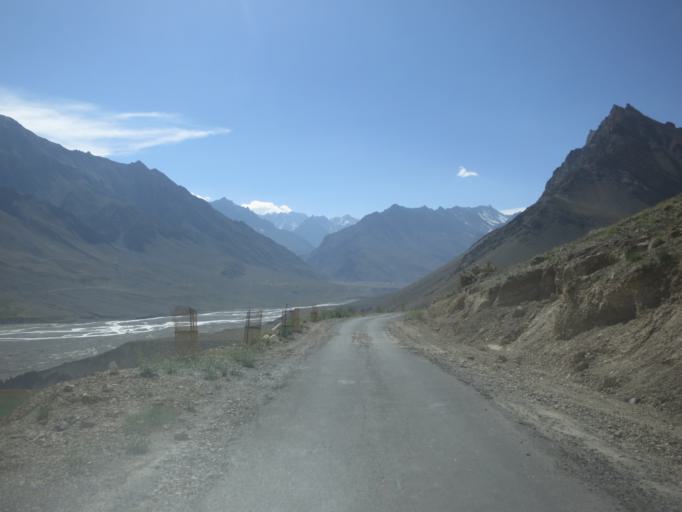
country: IN
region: Himachal Pradesh
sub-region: Shimla
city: Sarahan
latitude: 32.3027
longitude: 78.0063
